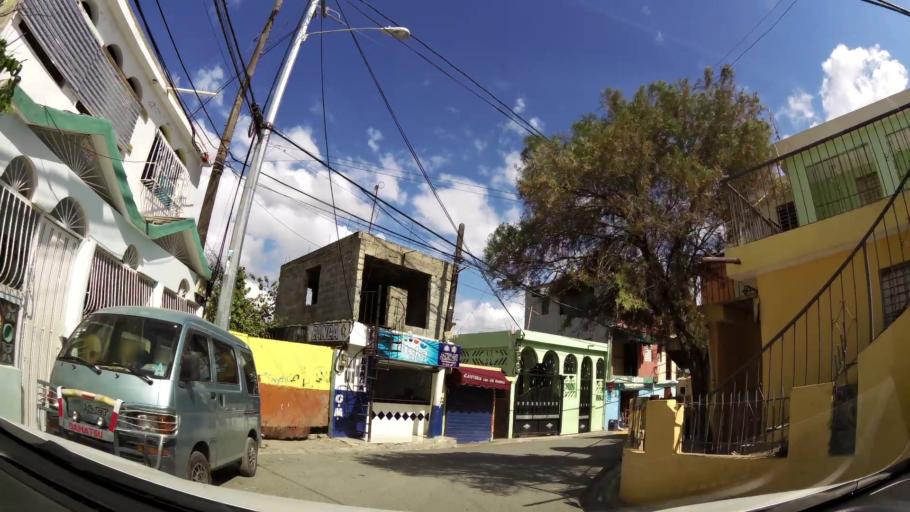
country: DO
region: Nacional
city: Ensanche Luperon
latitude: 18.5413
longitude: -69.9015
